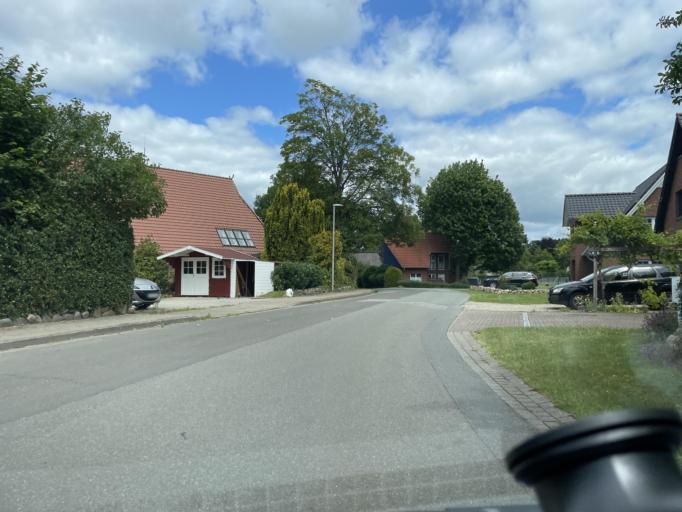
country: DE
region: Lower Saxony
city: Buxtehude
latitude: 53.4549
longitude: 9.7080
